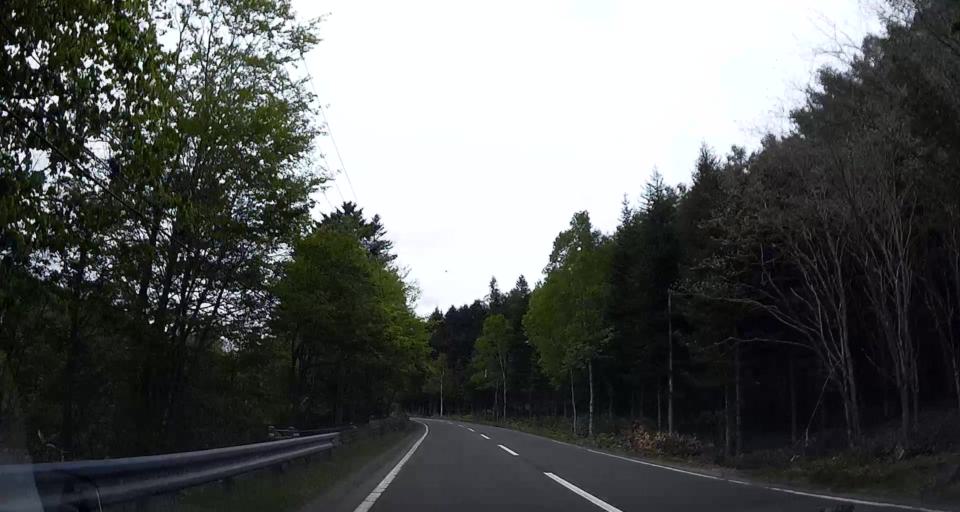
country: JP
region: Hokkaido
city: Shiraoi
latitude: 42.6802
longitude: 141.0985
